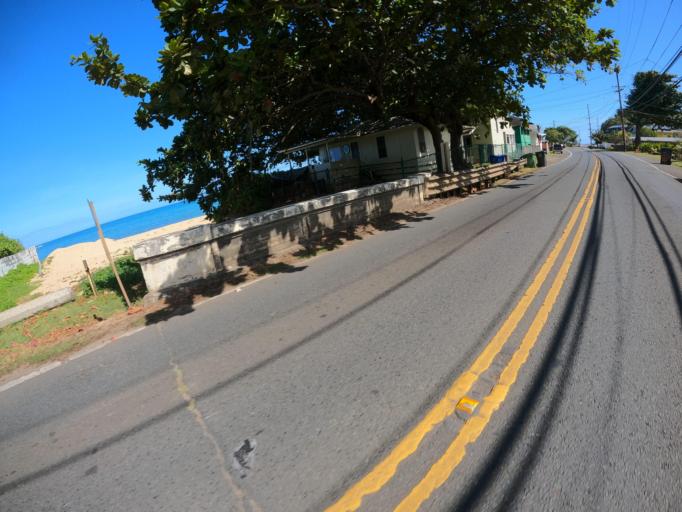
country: US
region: Hawaii
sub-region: Honolulu County
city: Hau'ula
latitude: 21.6071
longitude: -157.9068
